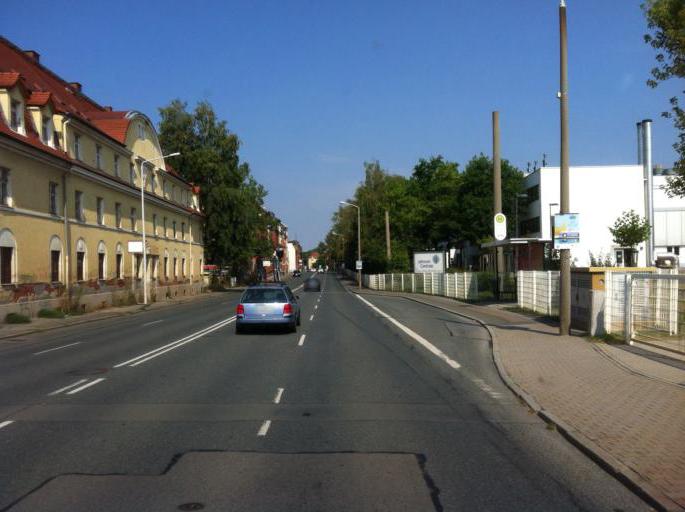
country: DE
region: Saxony
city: Weissenborn
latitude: 50.7095
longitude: 12.4671
